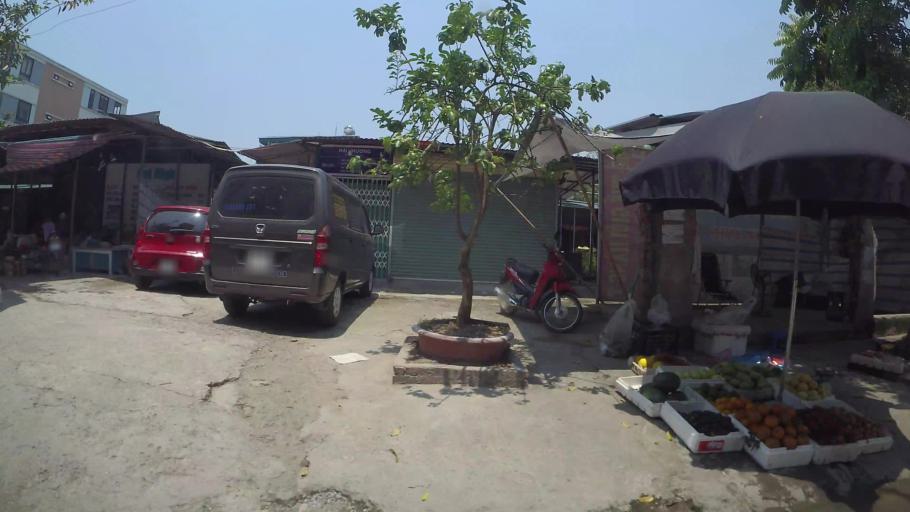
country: VN
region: Ha Noi
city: Hoan Kiem
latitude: 21.0261
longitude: 105.8930
